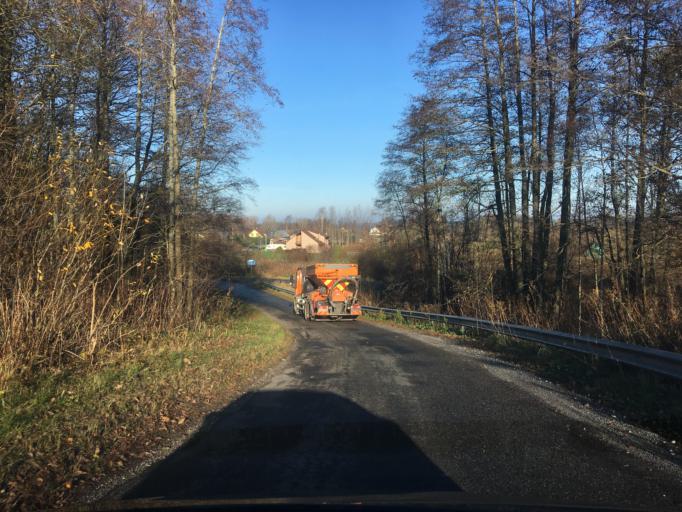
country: EE
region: Harju
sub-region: Maardu linn
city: Maardu
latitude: 59.4751
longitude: 25.1184
